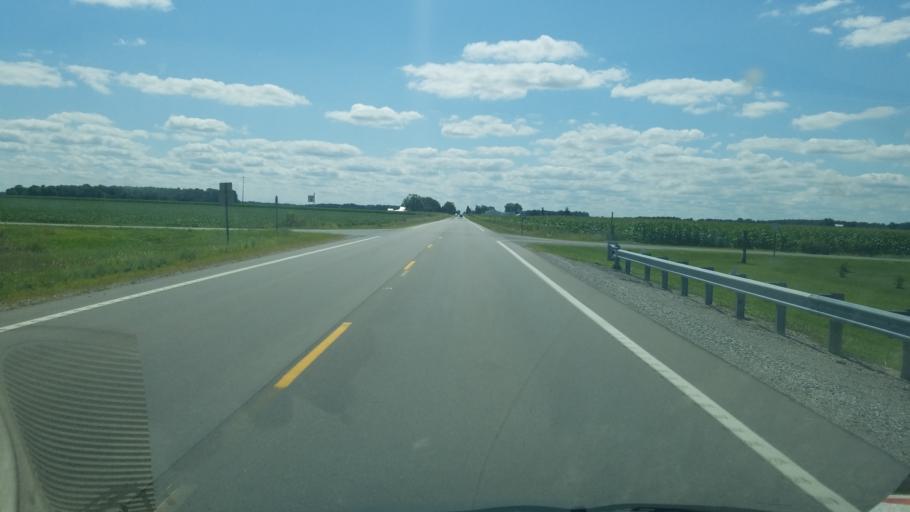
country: US
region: Ohio
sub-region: Fulton County
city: Delta
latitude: 41.6860
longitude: -84.0364
